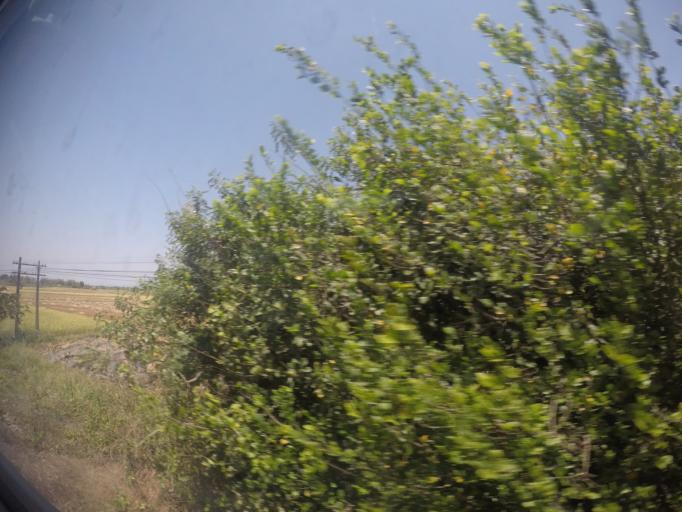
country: VN
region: Binh Thuan
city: Cho Lau
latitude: 11.2529
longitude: 108.5210
